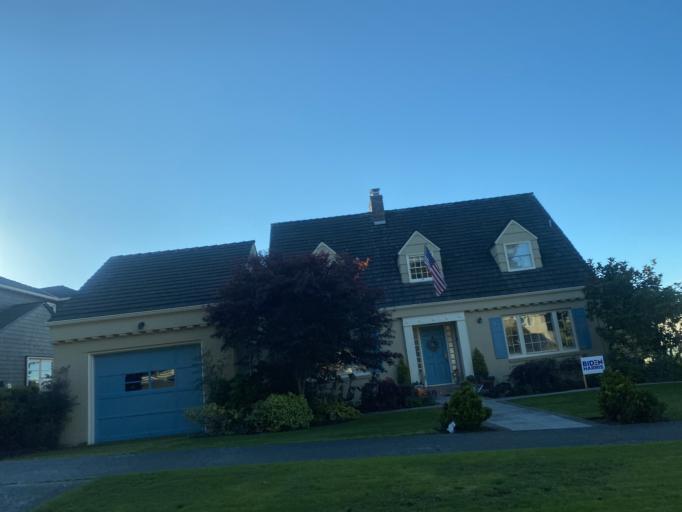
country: US
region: Washington
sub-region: King County
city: Seattle
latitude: 47.6477
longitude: -122.4120
